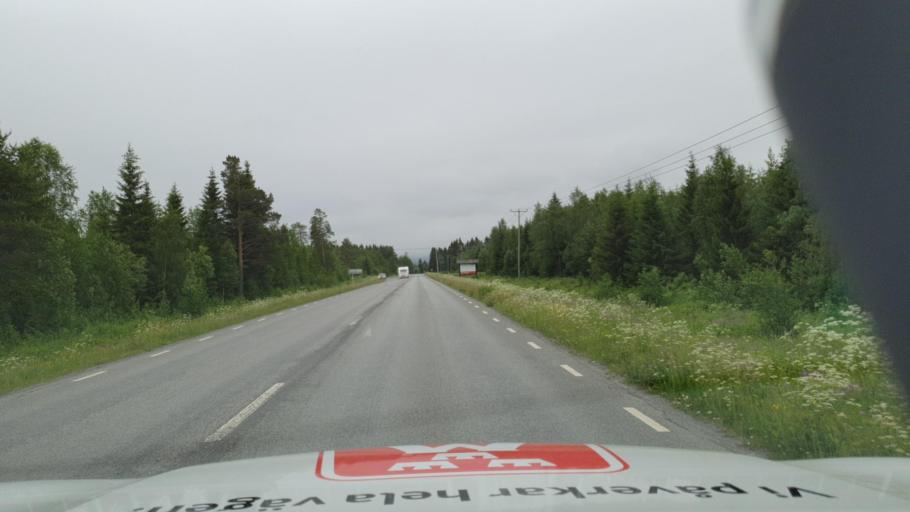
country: SE
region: Jaemtland
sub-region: Are Kommun
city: Jarpen
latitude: 63.3680
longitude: 13.4342
